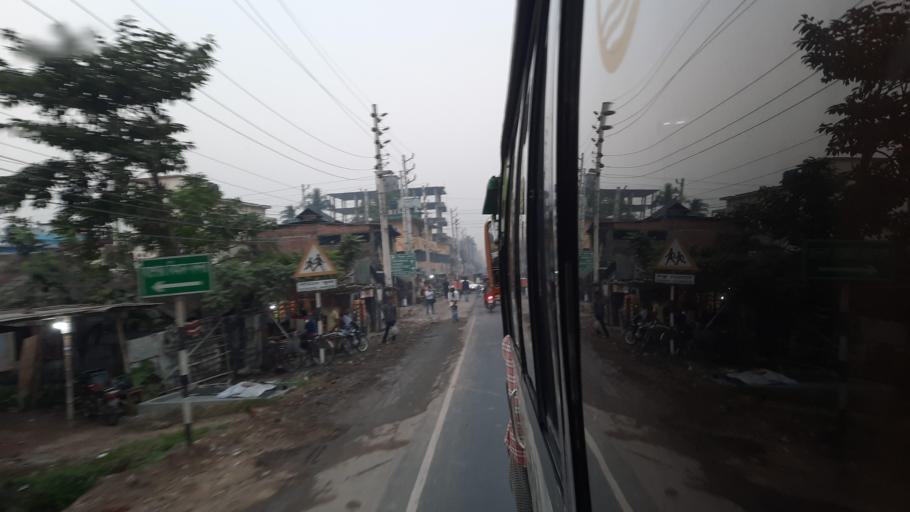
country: BD
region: Khulna
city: Jessore
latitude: 23.1709
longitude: 89.1927
